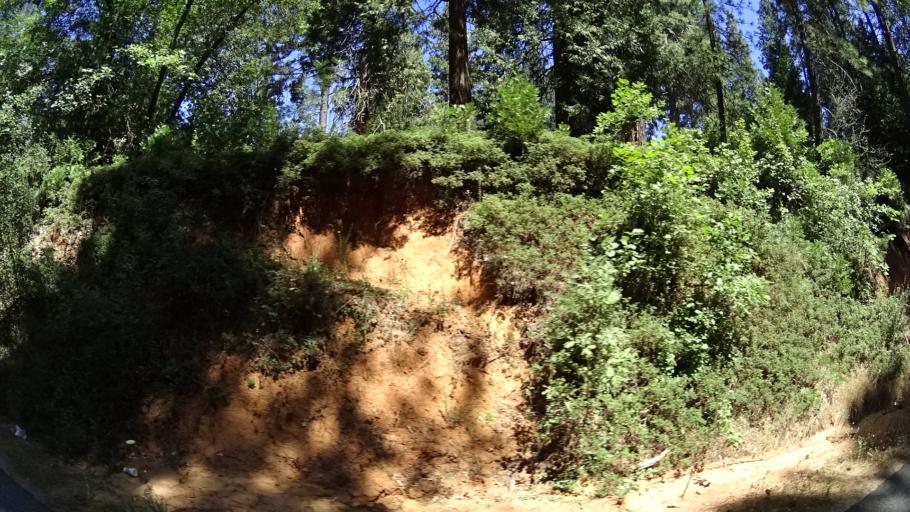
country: US
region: California
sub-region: Amador County
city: Pioneer
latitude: 38.4079
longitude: -120.5164
